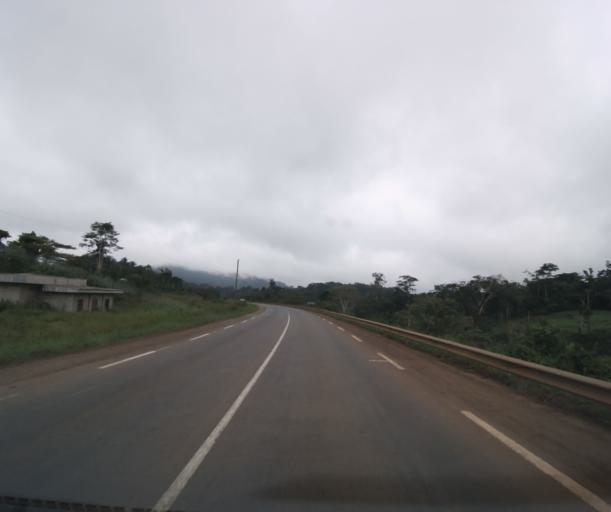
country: CM
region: Centre
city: Mbankomo
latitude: 3.7644
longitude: 11.1125
